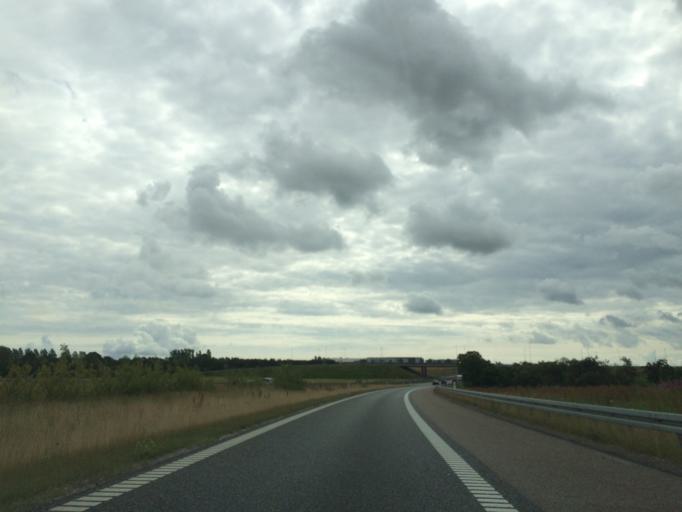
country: DK
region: Central Jutland
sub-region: Arhus Kommune
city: Trige
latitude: 56.2220
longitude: 10.1262
